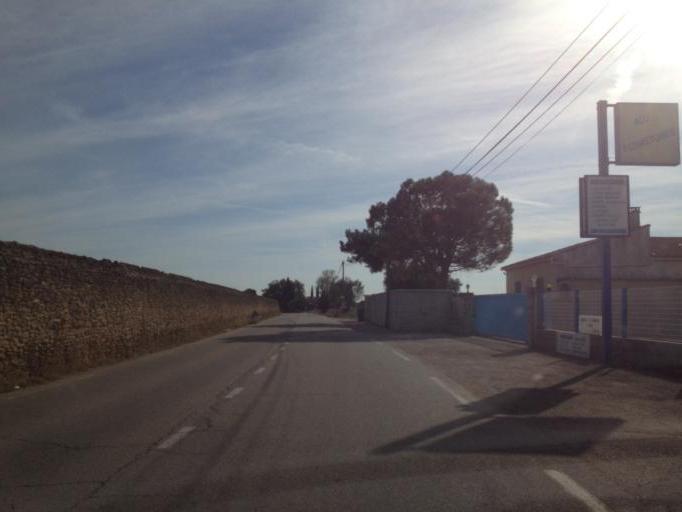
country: FR
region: Provence-Alpes-Cote d'Azur
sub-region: Departement du Vaucluse
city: Courthezon
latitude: 44.0961
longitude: 4.8798
